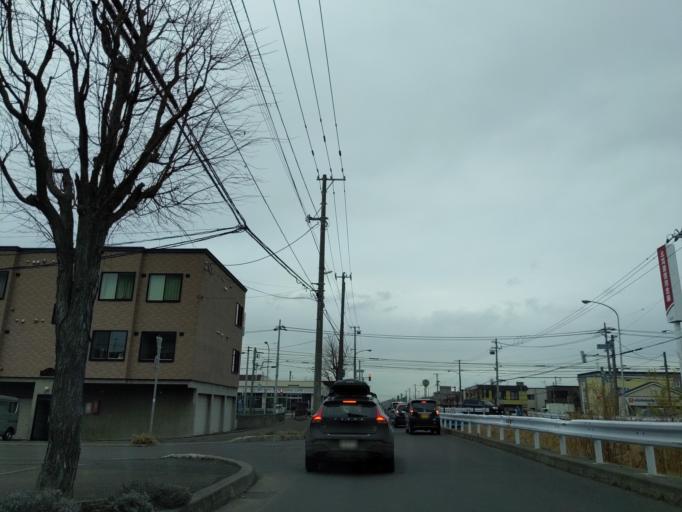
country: JP
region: Hokkaido
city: Sapporo
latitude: 43.1000
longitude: 141.4076
